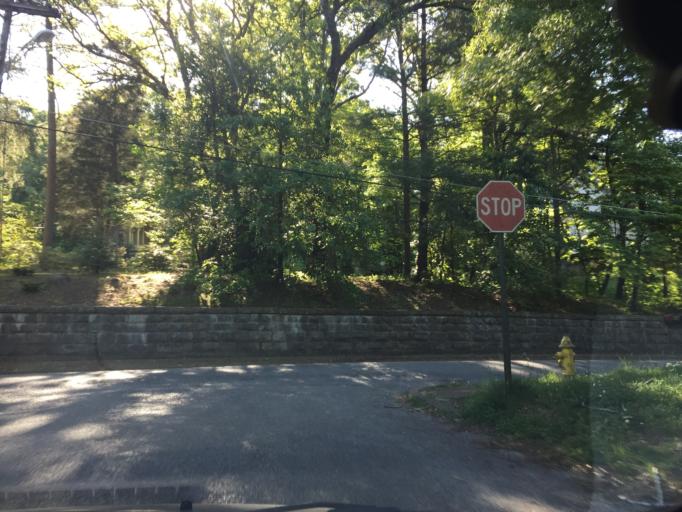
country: US
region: Tennessee
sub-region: Hamilton County
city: Lookout Mountain
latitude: 34.9944
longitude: -85.3265
